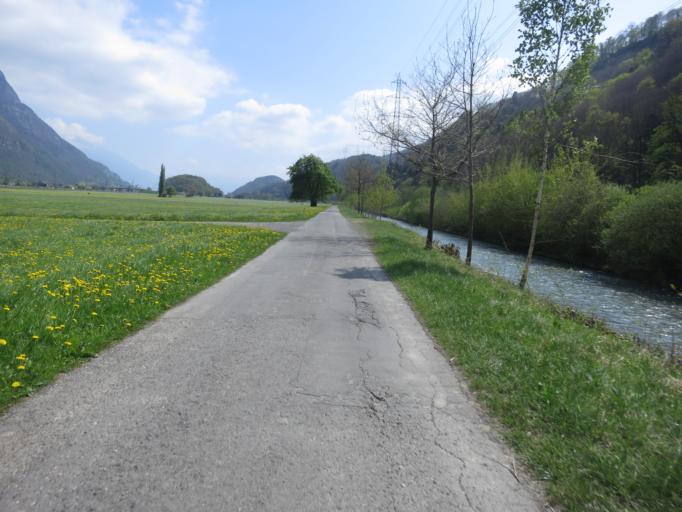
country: CH
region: Saint Gallen
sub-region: Wahlkreis Sarganserland
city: Flums
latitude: 47.0720
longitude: 9.3748
